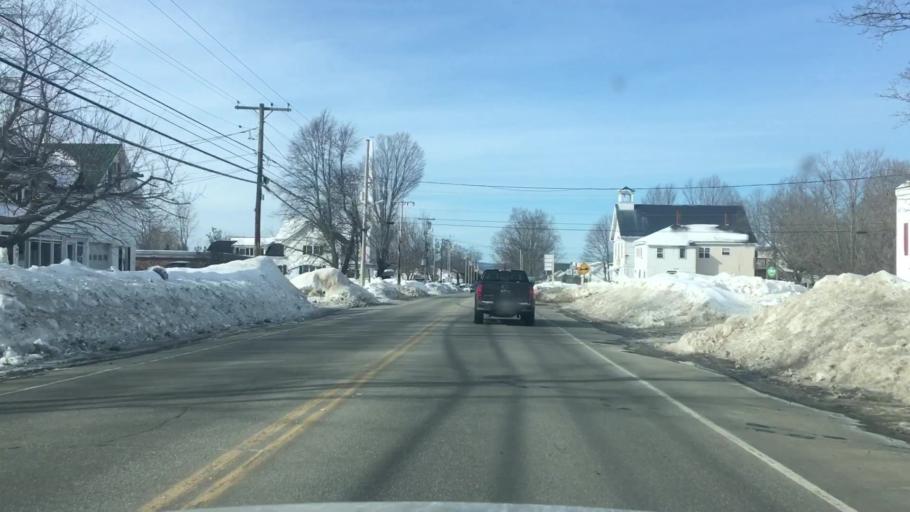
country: US
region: Maine
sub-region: Penobscot County
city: Charleston
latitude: 45.0009
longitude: -69.0221
